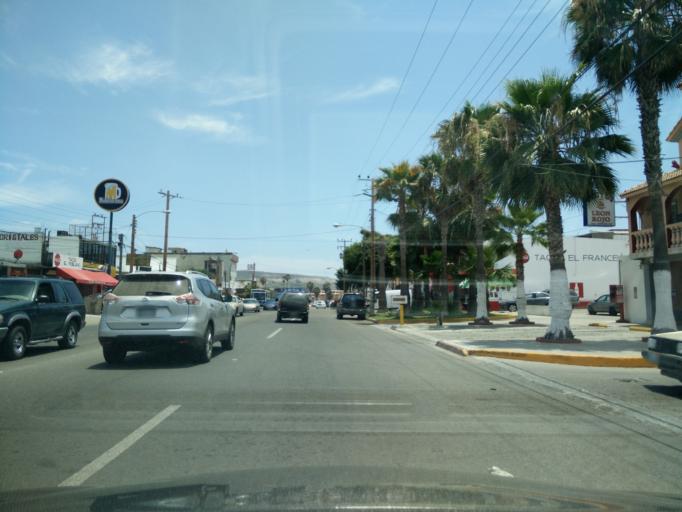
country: MX
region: Baja California
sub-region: Tijuana
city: La Esperanza [Granjas Familiares]
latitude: 32.5135
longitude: -117.1201
